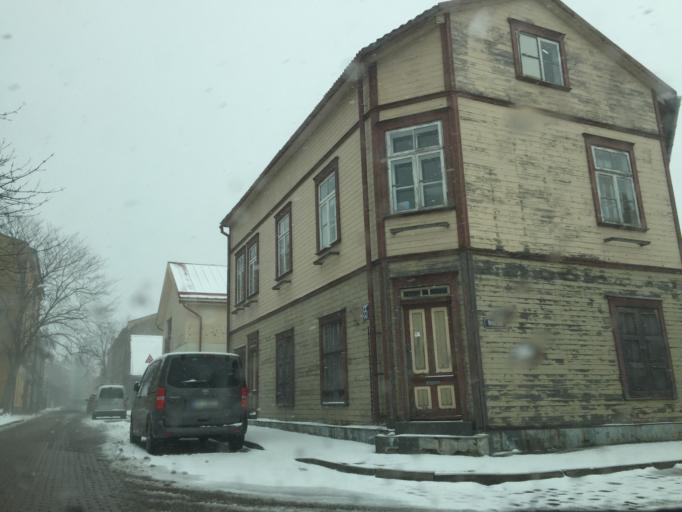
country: LV
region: Ventspils
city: Ventspils
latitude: 57.3953
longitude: 21.5585
